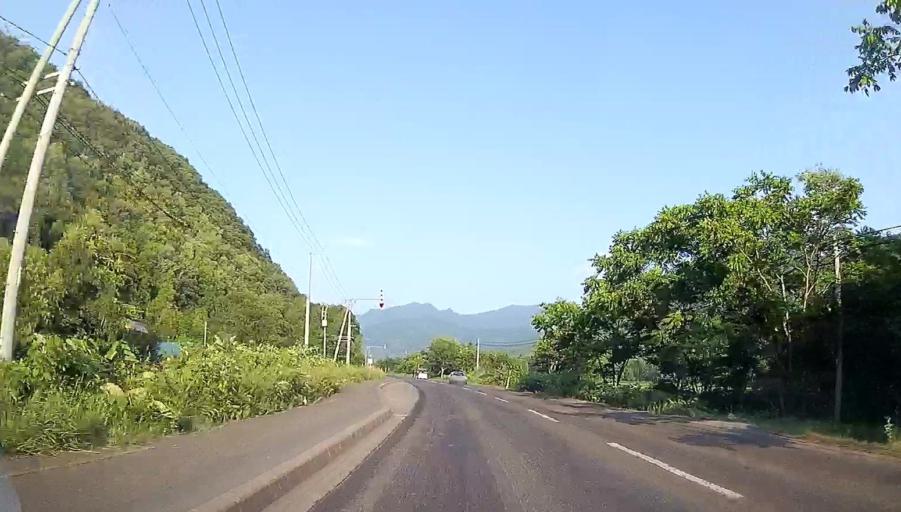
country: JP
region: Hokkaido
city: Shimo-furano
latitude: 42.8945
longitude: 142.5061
